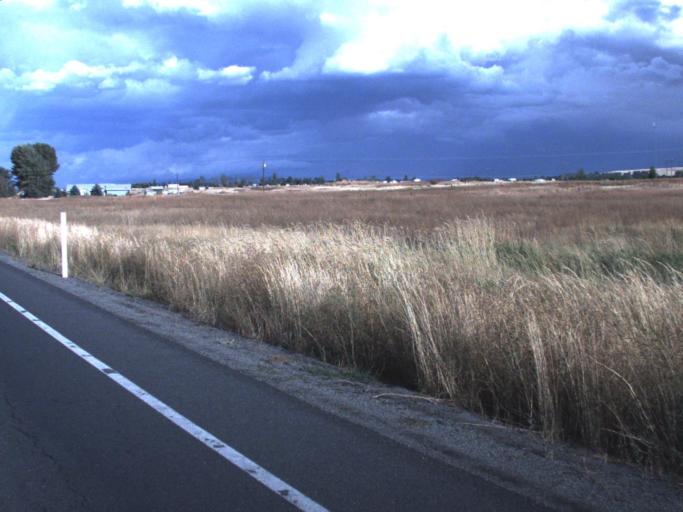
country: US
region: Washington
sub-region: Spokane County
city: Fairchild Air Force Base
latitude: 47.5901
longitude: -117.6325
